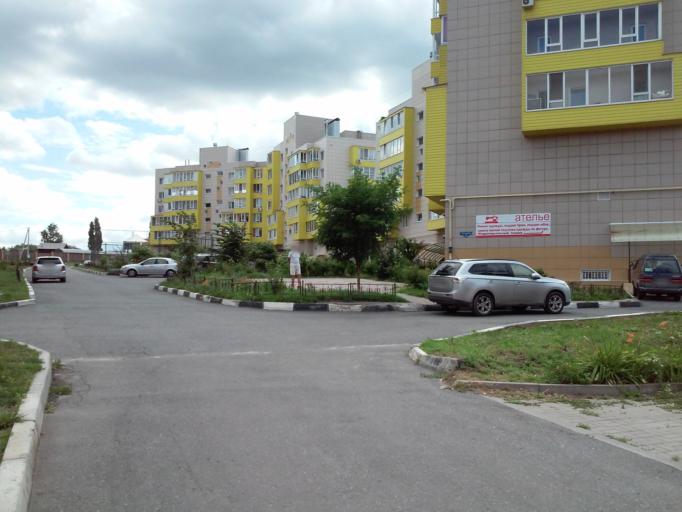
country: RU
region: Belgorod
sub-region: Belgorodskiy Rayon
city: Belgorod
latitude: 50.5357
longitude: 36.5760
